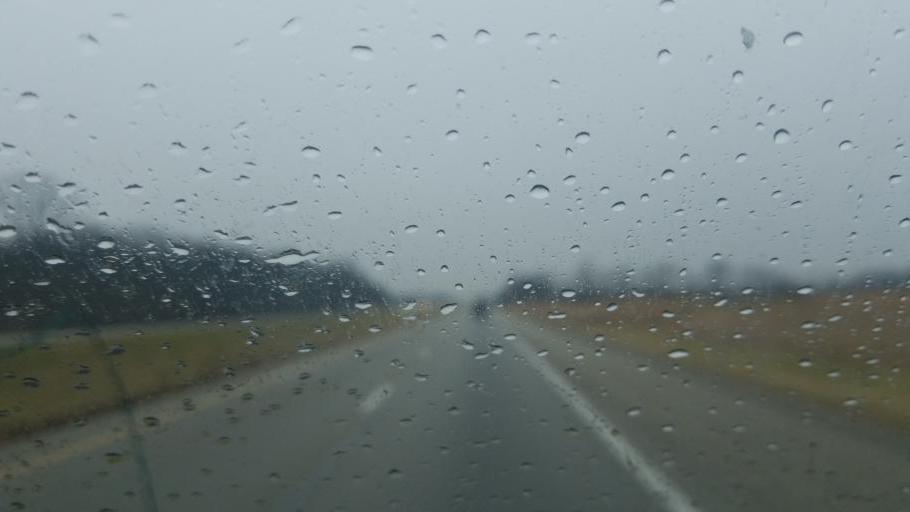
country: US
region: Ohio
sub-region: Preble County
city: Lewisburg
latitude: 39.8379
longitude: -84.5078
